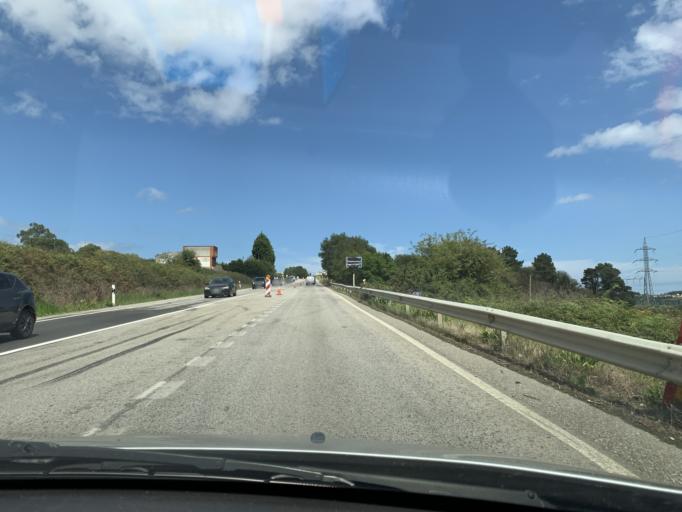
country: ES
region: Galicia
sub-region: Provincia de Lugo
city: Foz
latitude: 43.5483
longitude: -7.2692
